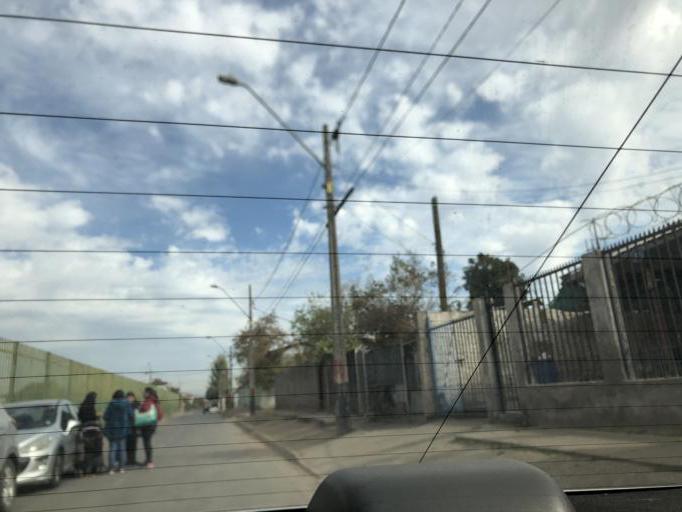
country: CL
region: Santiago Metropolitan
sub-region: Provincia de Cordillera
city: Puente Alto
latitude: -33.6106
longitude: -70.5181
